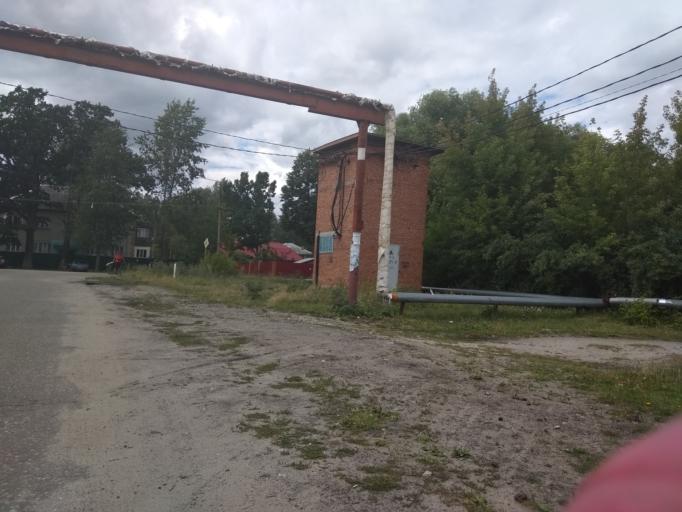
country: RU
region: Moskovskaya
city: Misheronskiy
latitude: 55.7201
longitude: 39.7415
